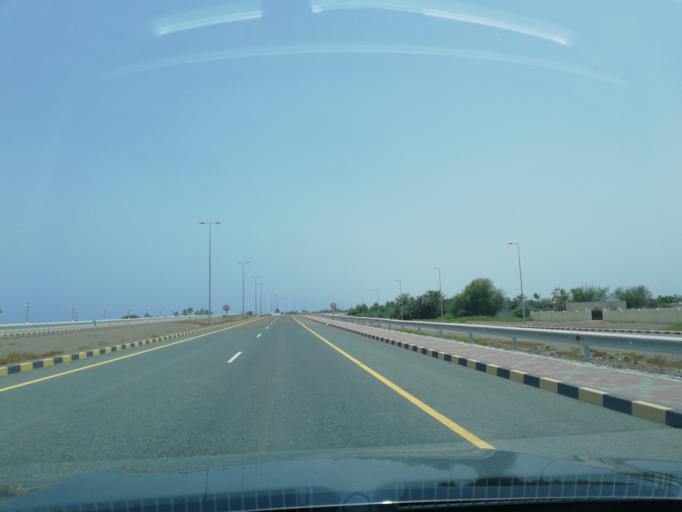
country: OM
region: Al Batinah
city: Shinas
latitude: 24.8060
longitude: 56.4482
